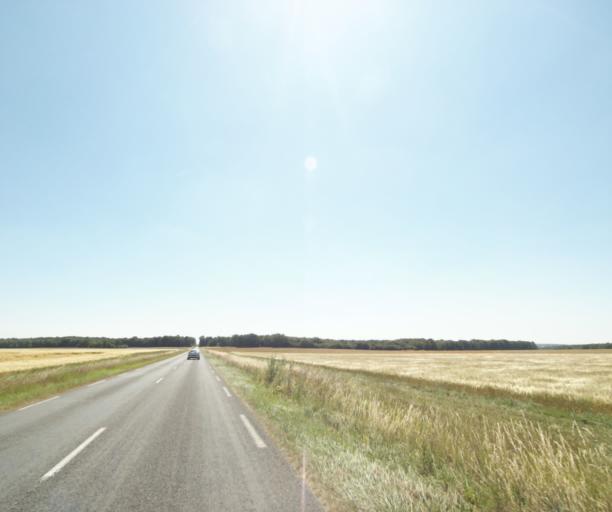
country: FR
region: Centre
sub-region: Departement du Loiret
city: Malesherbes
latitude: 48.3216
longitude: 2.4442
